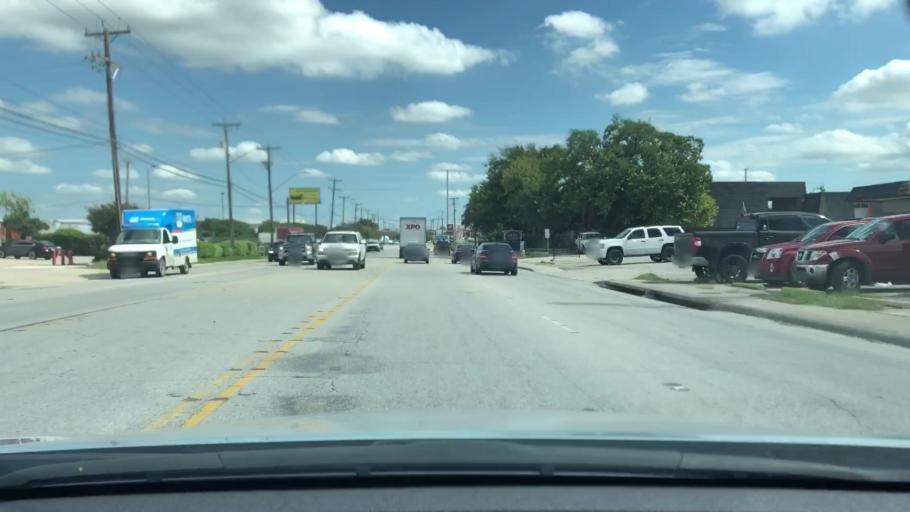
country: US
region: Texas
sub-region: Bexar County
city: Kirby
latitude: 29.4841
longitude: -98.3969
